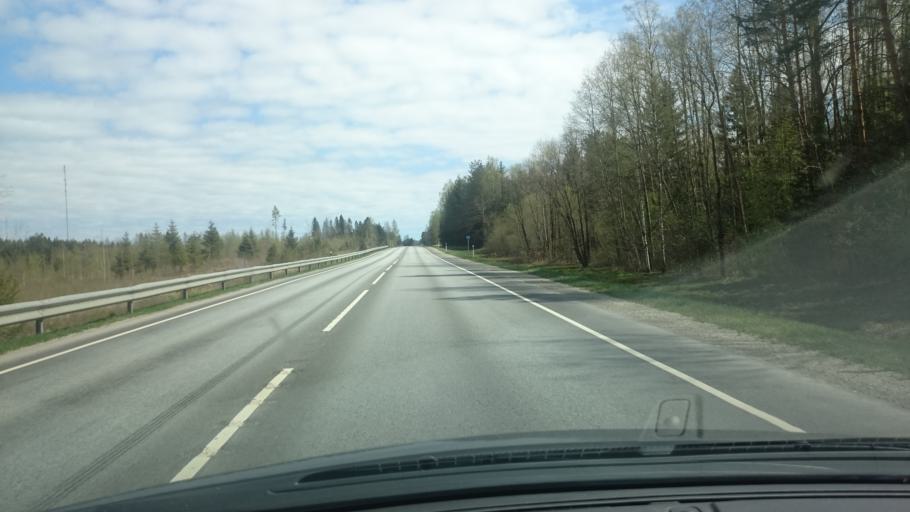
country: EE
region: Laeaene-Virumaa
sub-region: Viru-Nigula vald
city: Kunda
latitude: 59.3764
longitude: 26.5895
